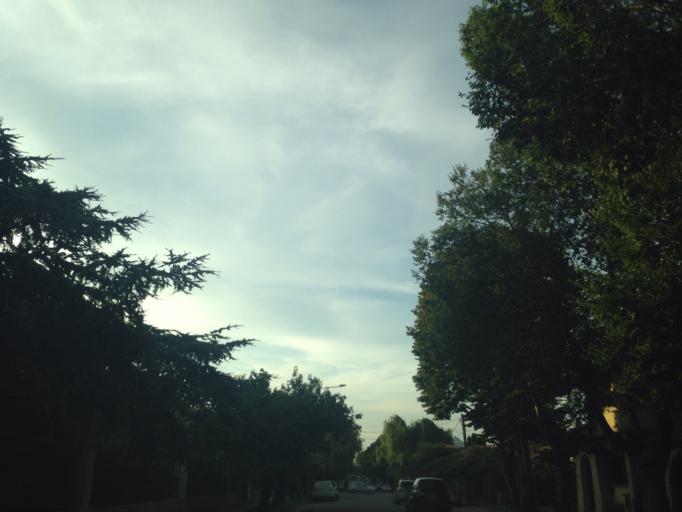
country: AR
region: Buenos Aires
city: Mar del Plata
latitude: -38.0209
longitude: -57.5401
